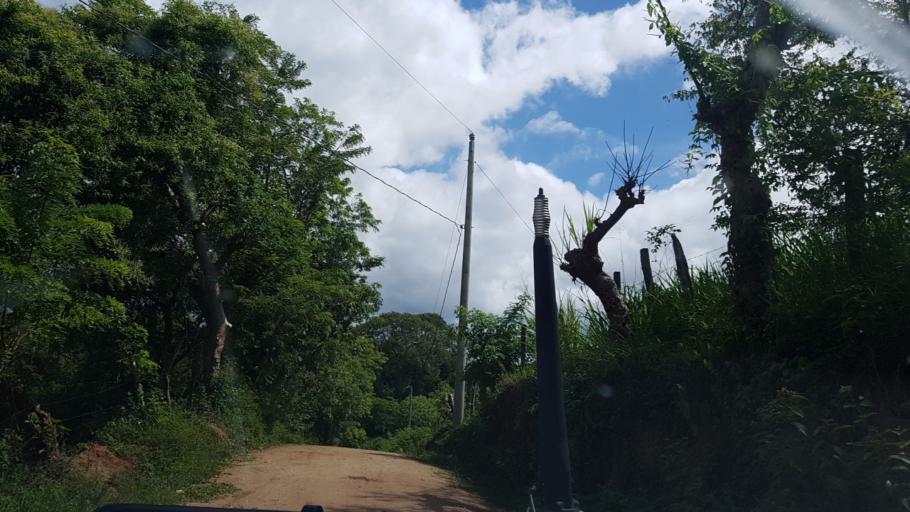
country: NI
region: Nueva Segovia
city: Ciudad Antigua
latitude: 13.6513
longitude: -86.2406
